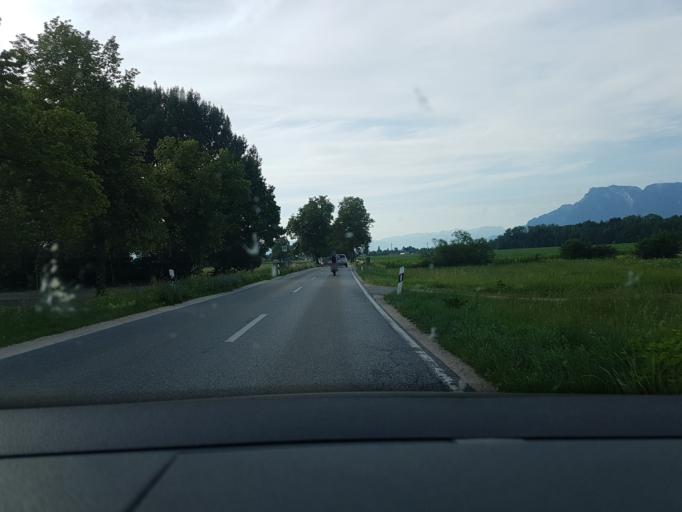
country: DE
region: Bavaria
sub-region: Upper Bavaria
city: Ainring
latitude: 47.8453
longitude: 12.9480
